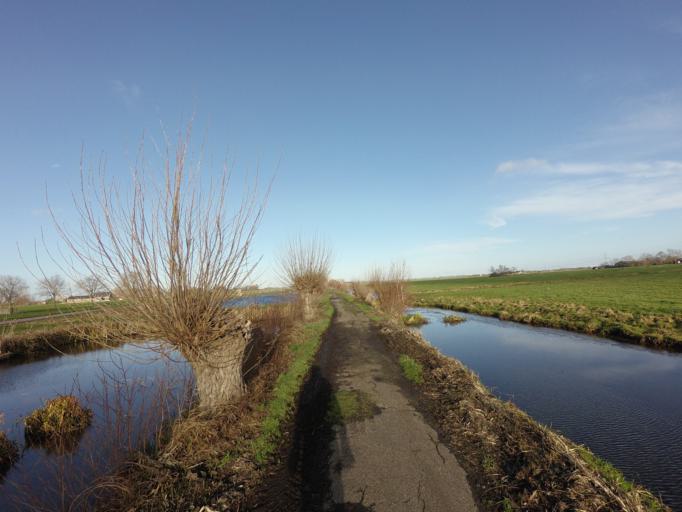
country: NL
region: Utrecht
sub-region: Stichtse Vecht
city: Breukelen
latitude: 52.1902
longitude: 4.9705
